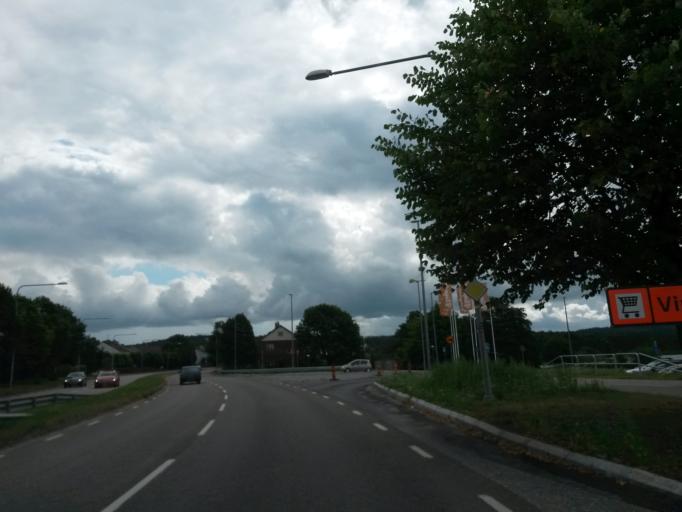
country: SE
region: Vaestra Goetaland
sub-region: Alingsas Kommun
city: Alingsas
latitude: 57.9246
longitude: 12.5469
